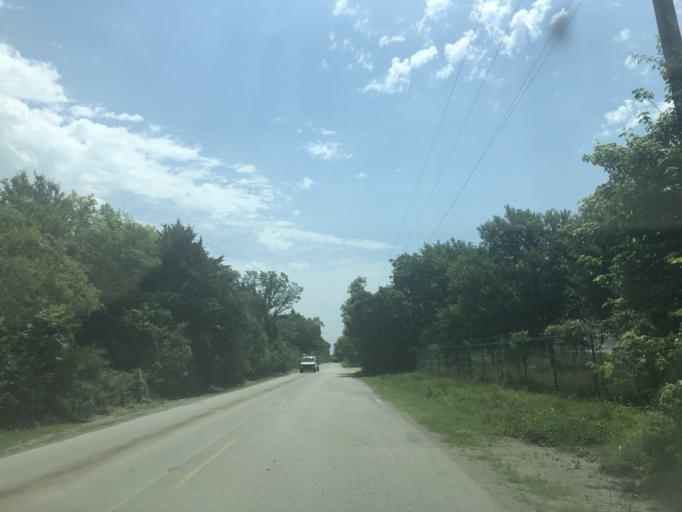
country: US
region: Texas
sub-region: Dallas County
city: Irving
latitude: 32.7866
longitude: -96.9460
